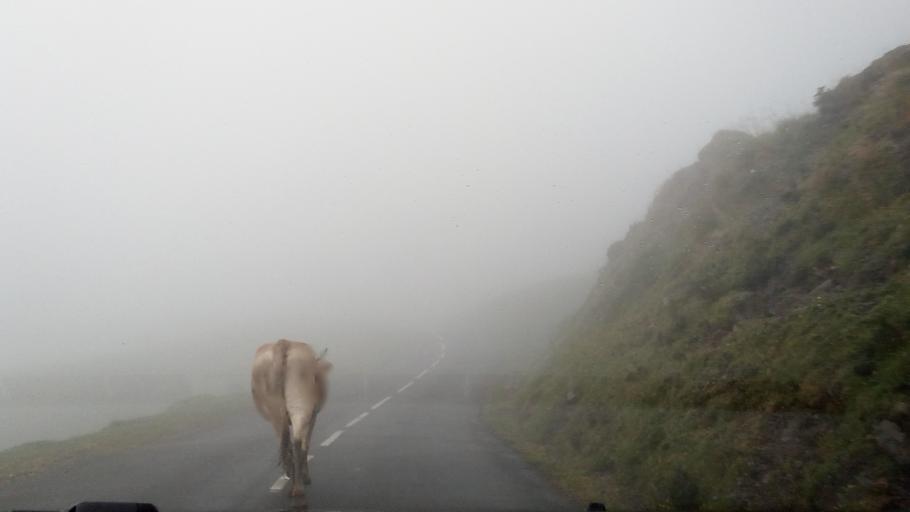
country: FR
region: Aquitaine
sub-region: Departement des Pyrenees-Atlantiques
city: Laruns
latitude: 42.9720
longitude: -0.3305
